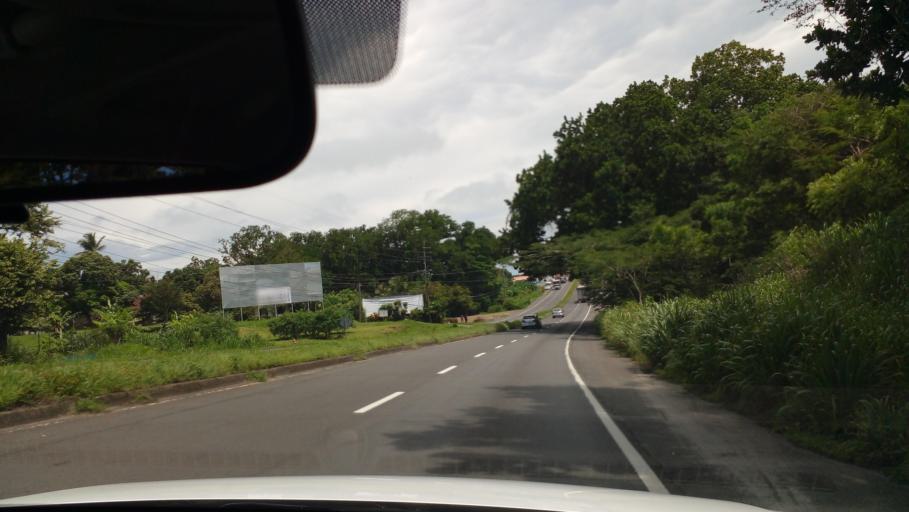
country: PA
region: Panama
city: Nueva Gorgona
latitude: 8.4777
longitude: -79.9586
